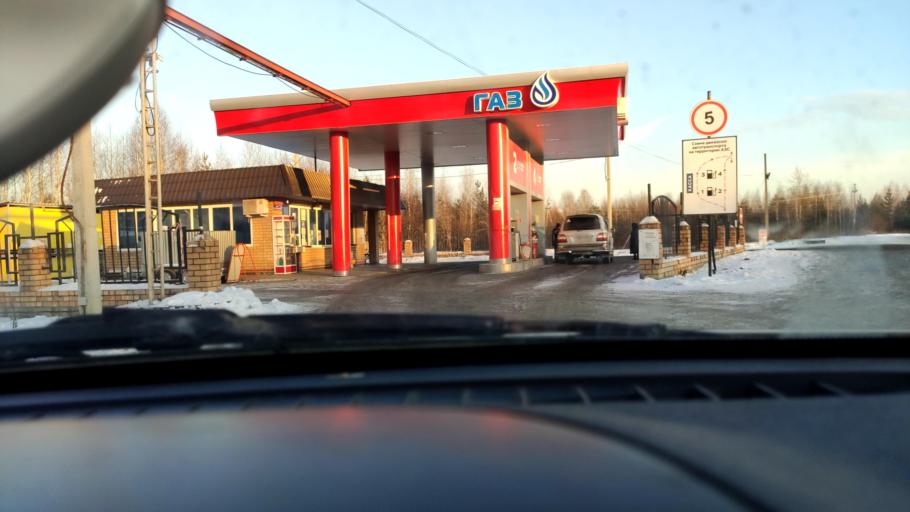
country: RU
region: Perm
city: Perm
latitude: 58.0923
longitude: 56.3157
